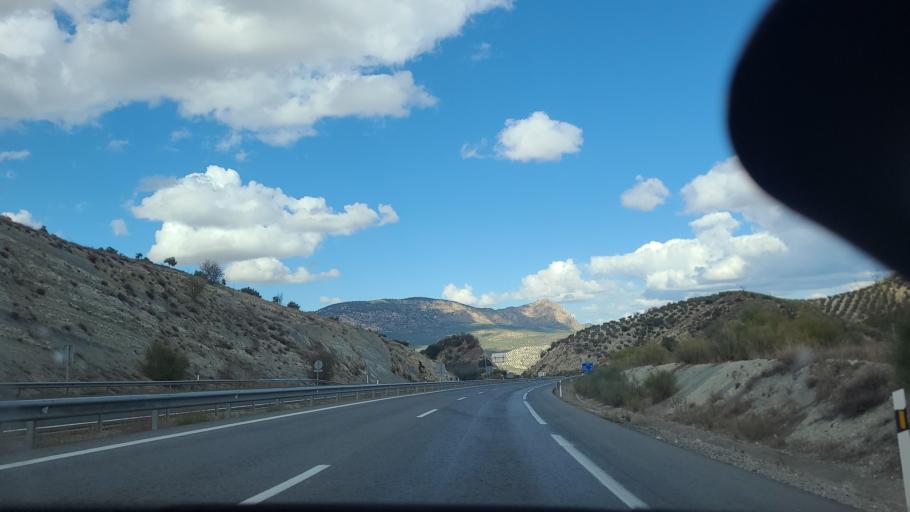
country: ES
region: Andalusia
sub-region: Provincia de Jaen
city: Campillo de Arenas
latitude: 37.5390
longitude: -3.6358
